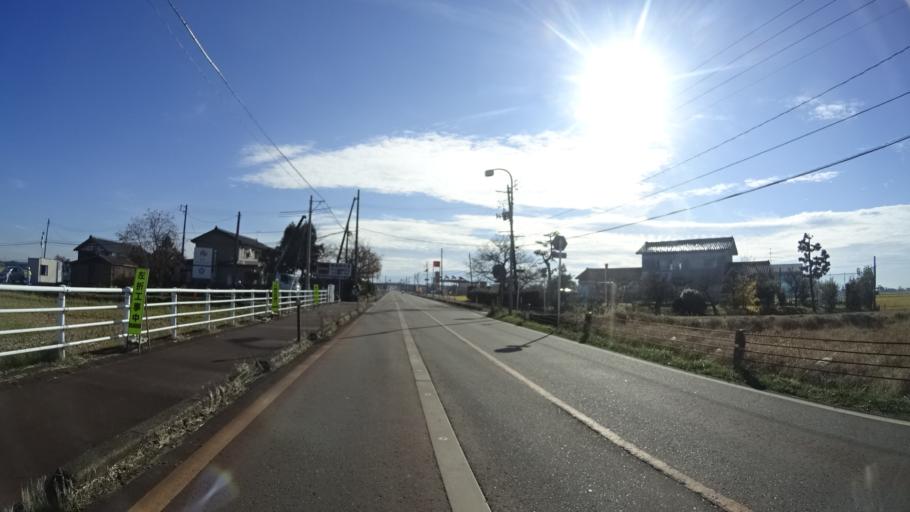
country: JP
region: Niigata
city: Mitsuke
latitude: 37.5513
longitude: 138.8677
